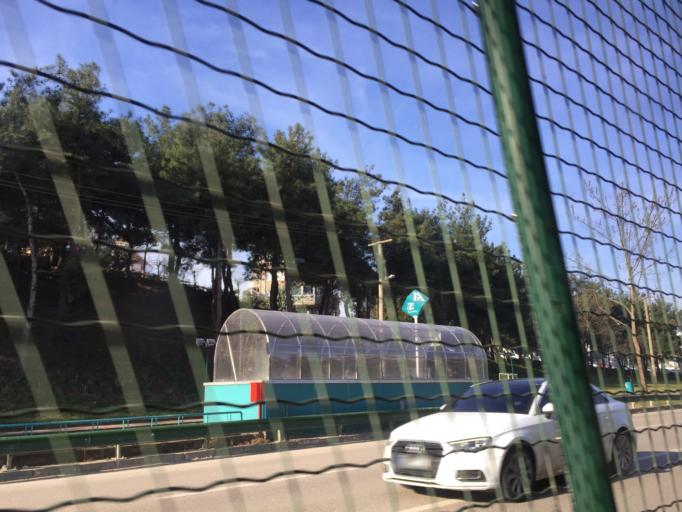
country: TR
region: Bursa
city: Yildirim
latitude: 40.2292
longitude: 28.9864
